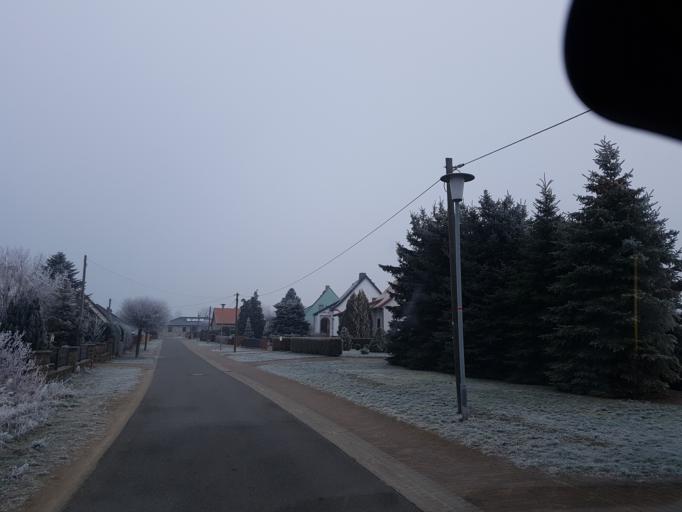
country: DE
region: Brandenburg
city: Muhlberg
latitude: 51.4361
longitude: 13.2282
